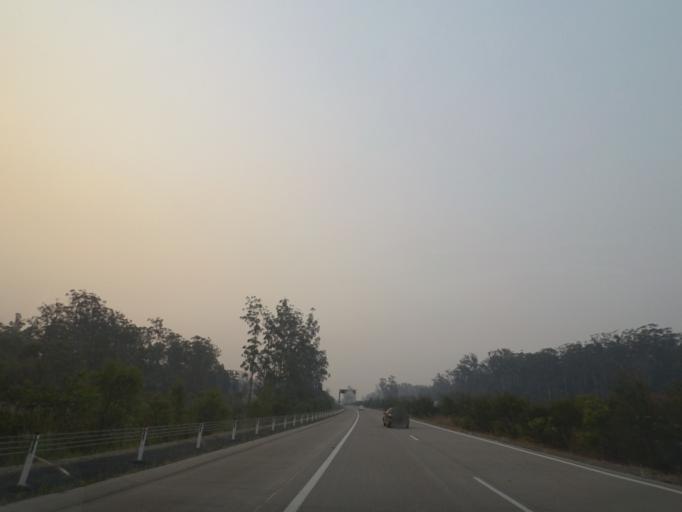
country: AU
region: New South Wales
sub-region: Nambucca Shire
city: Macksville
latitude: -30.8673
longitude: 152.9279
